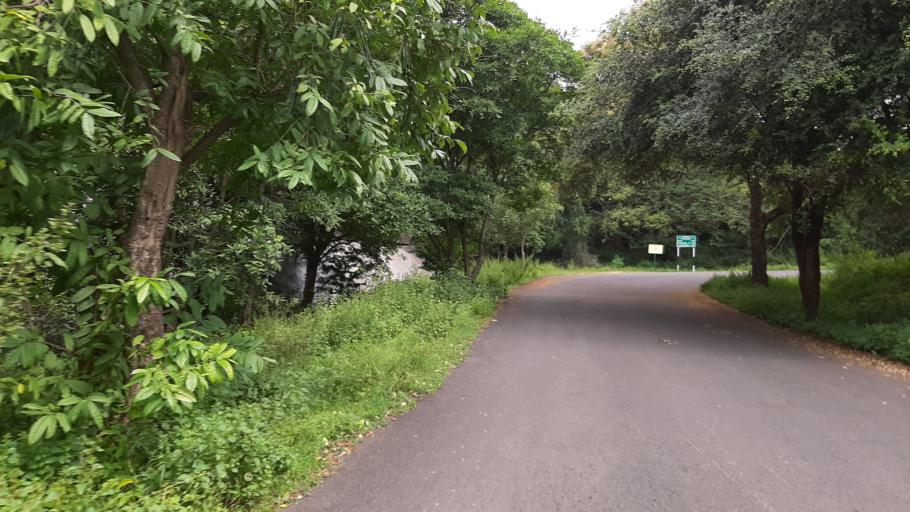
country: IN
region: Karnataka
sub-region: Ramanagara
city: Magadi
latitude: 12.9063
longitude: 77.2914
